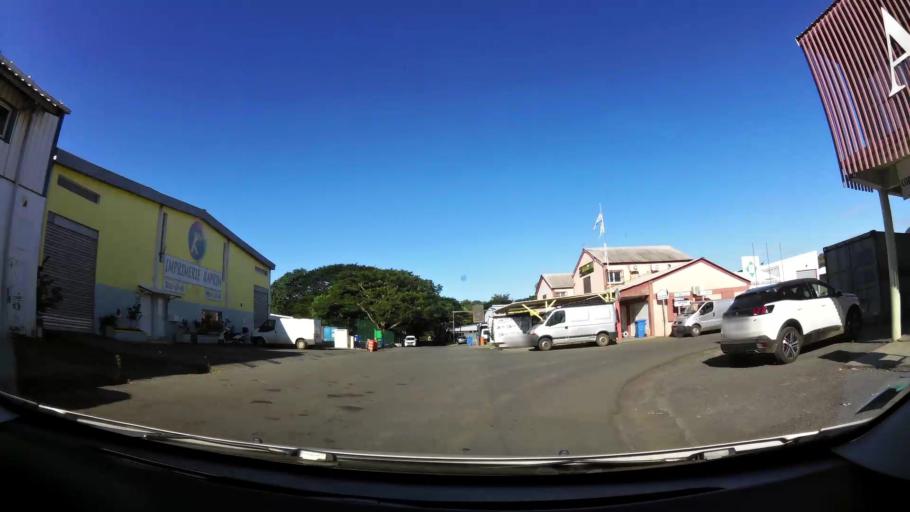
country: YT
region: Mamoudzou
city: Mamoudzou
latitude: -12.7663
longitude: 45.2291
